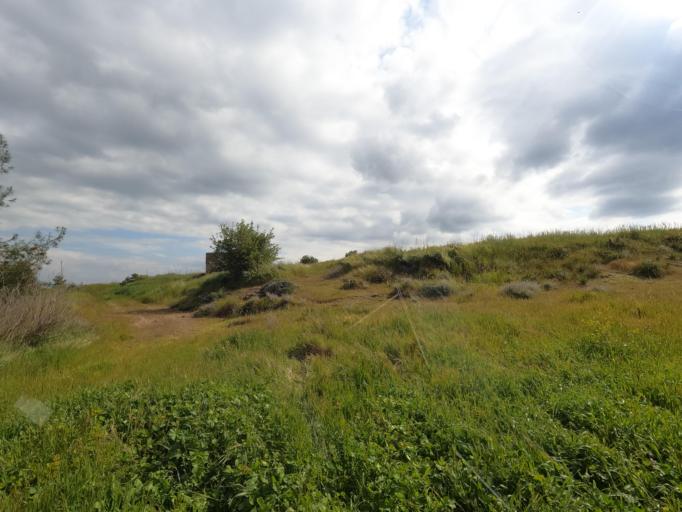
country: CY
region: Lefkosia
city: Kakopetria
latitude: 35.0770
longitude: 32.9558
